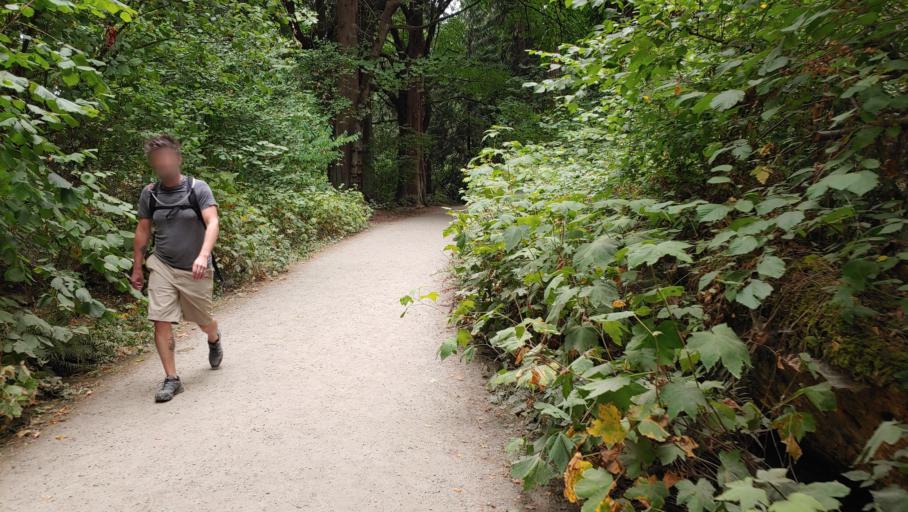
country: US
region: Washington
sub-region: King County
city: Mercer Island
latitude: 47.5538
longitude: -122.2501
